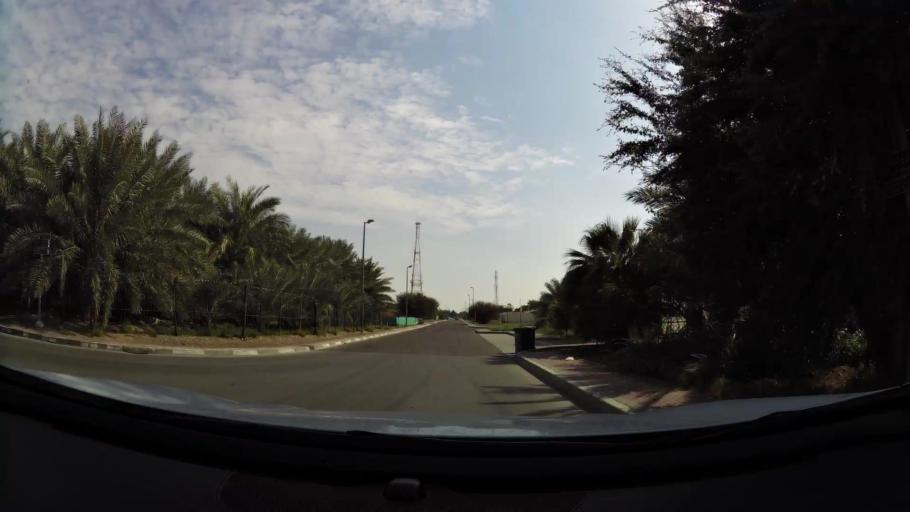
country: AE
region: Abu Dhabi
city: Al Ain
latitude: 24.0980
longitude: 55.9140
